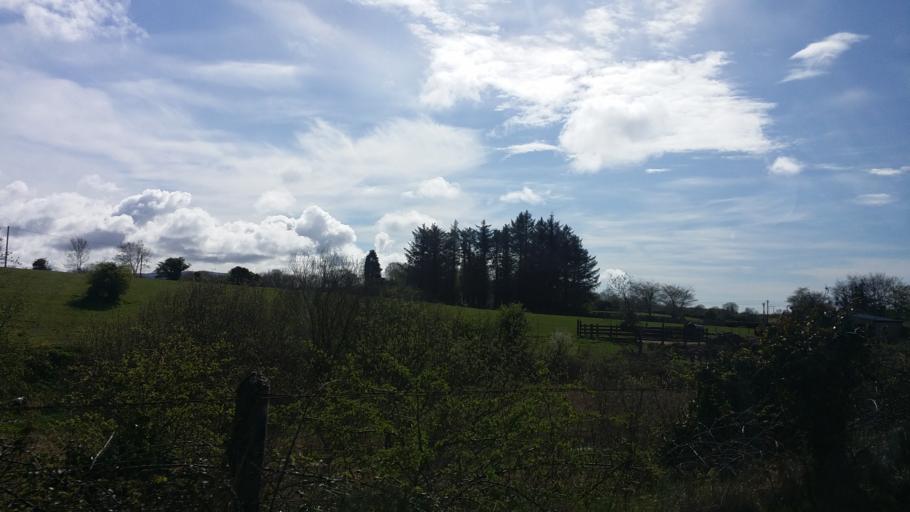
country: IE
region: Ulster
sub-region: County Donegal
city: Ballyshannon
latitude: 54.4927
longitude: -8.1593
